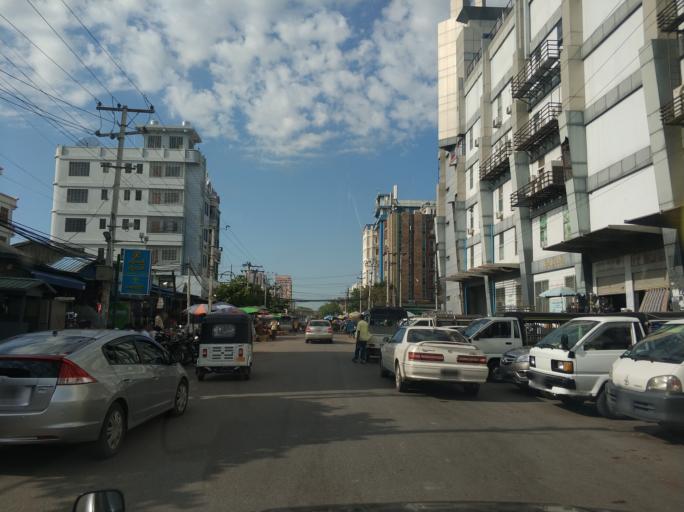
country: MM
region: Mandalay
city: Mandalay
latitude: 21.9713
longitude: 96.0882
